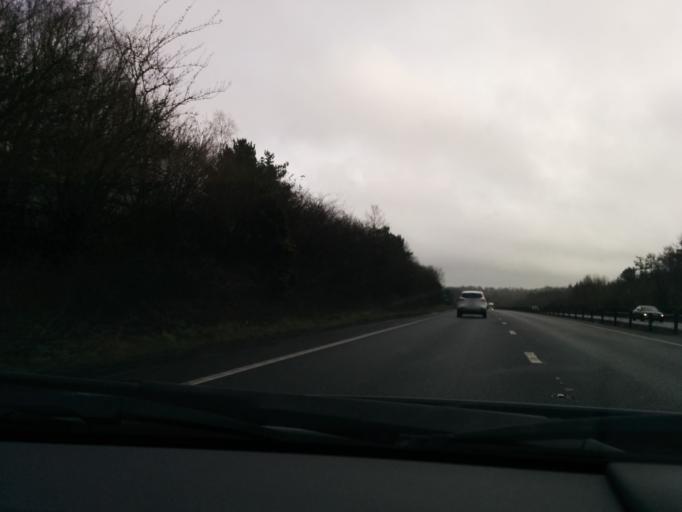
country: GB
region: England
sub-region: Hampshire
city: Highclere
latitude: 51.3612
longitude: -1.3535
